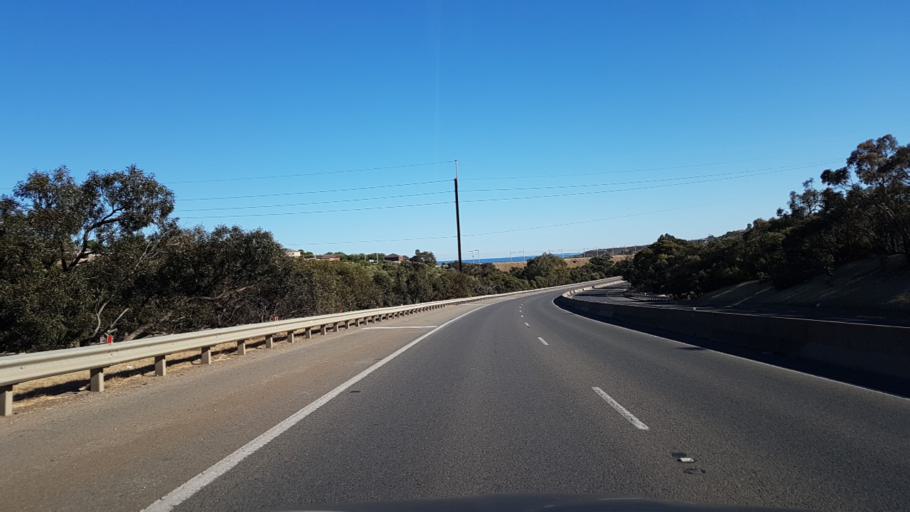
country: AU
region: South Australia
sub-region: Onkaparinga
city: Reynella
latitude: -35.0946
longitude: 138.4960
